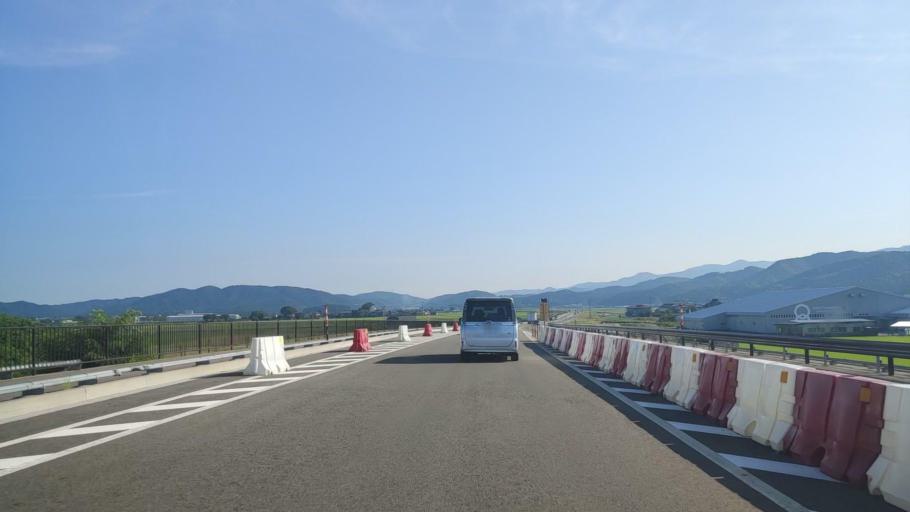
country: JP
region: Fukui
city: Maruoka
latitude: 36.1728
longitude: 136.2641
